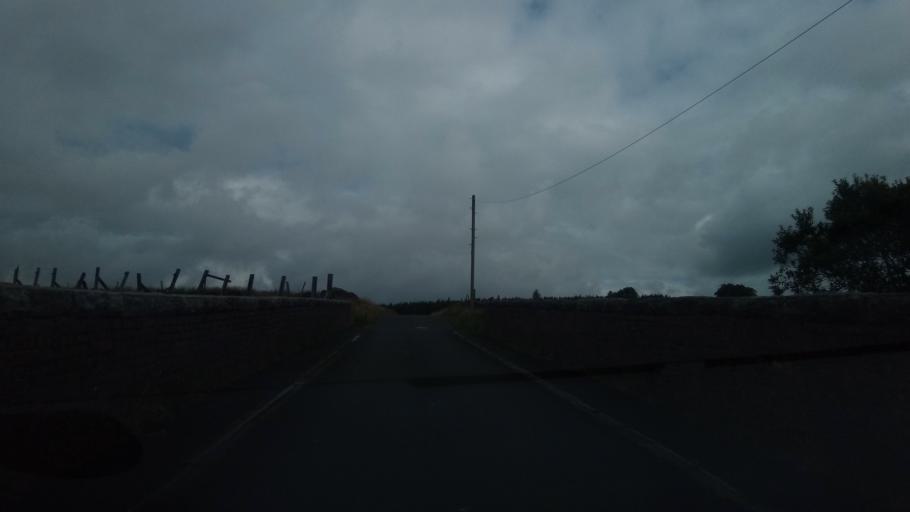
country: GB
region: England
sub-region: Cumbria
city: Sedbergh
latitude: 54.2834
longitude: -2.3642
